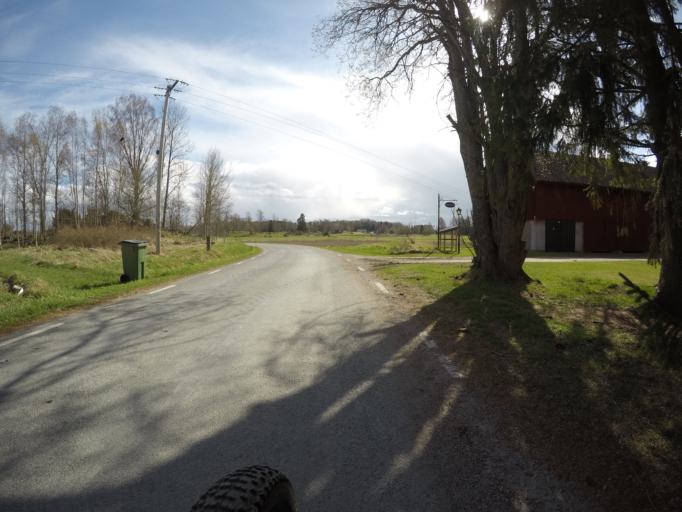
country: SE
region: Vaestmanland
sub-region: Kungsors Kommun
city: Kungsoer
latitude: 59.3015
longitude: 16.1381
